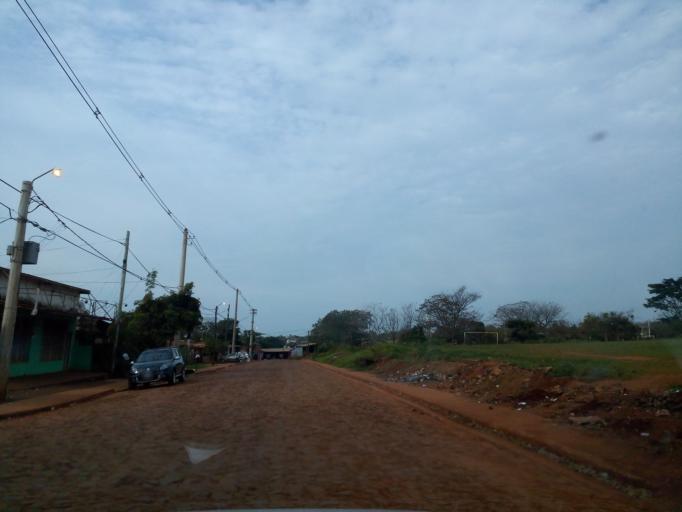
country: AR
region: Misiones
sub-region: Departamento de Capital
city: Posadas
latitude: -27.4230
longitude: -55.8945
